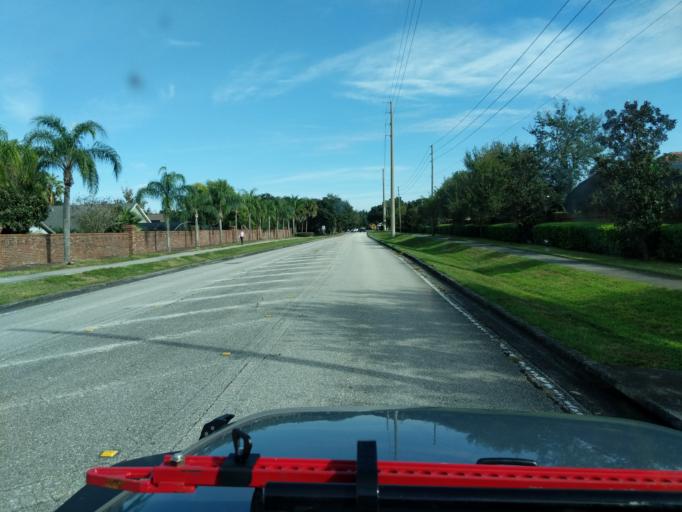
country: US
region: Florida
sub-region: Orange County
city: Gotha
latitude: 28.5298
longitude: -81.5358
